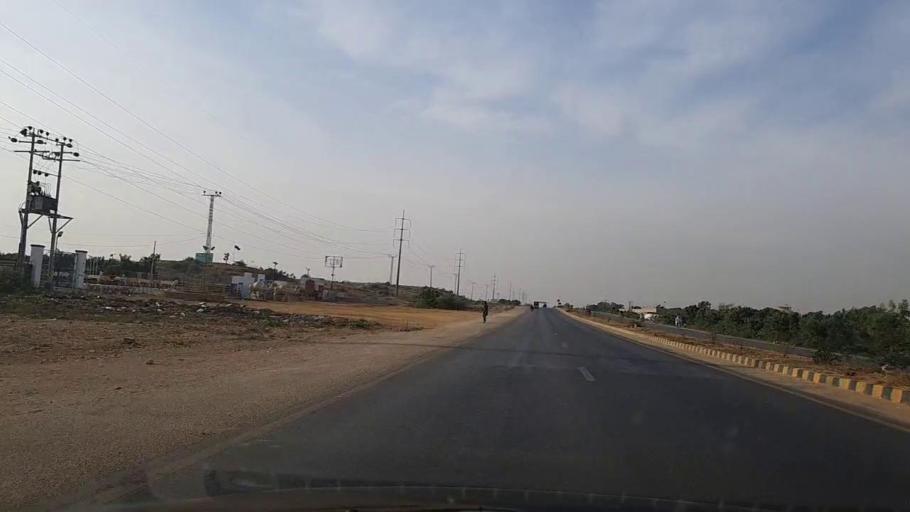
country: PK
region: Sindh
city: Gharo
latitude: 24.7592
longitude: 67.5594
